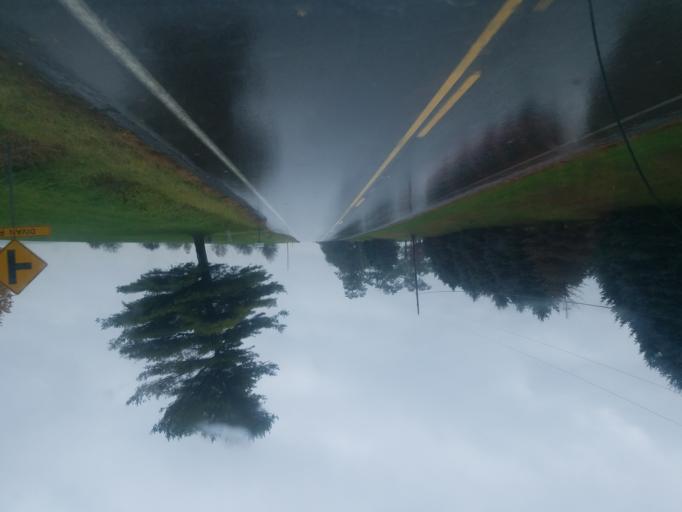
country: US
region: Ohio
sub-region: Licking County
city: Utica
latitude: 40.2650
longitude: -82.3493
